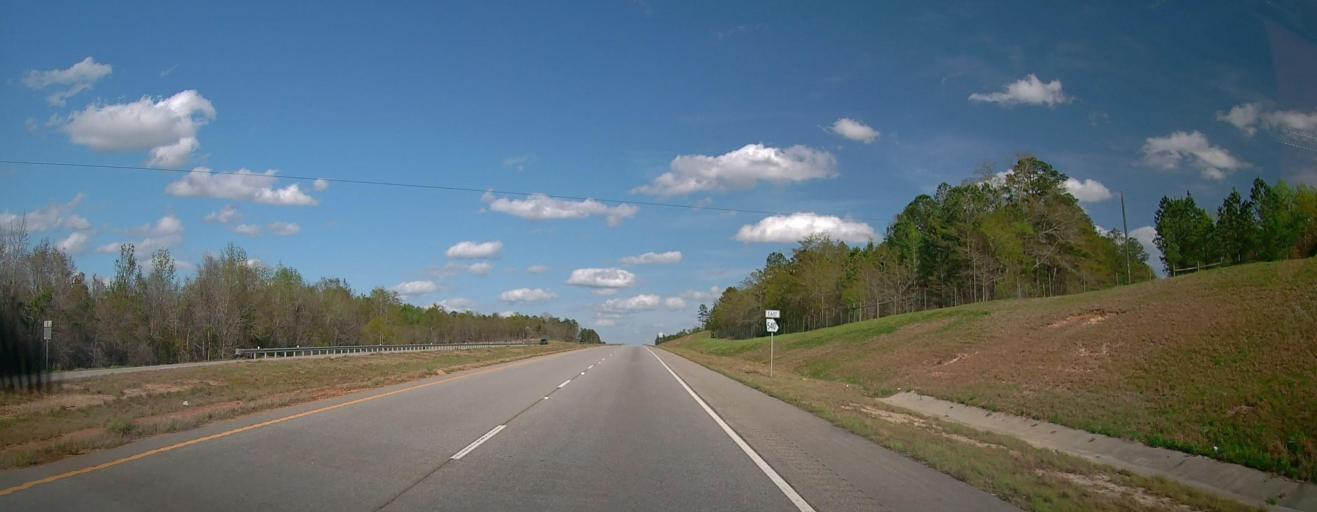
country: US
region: Georgia
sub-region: Baldwin County
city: Hardwick
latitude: 33.0374
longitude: -83.1475
